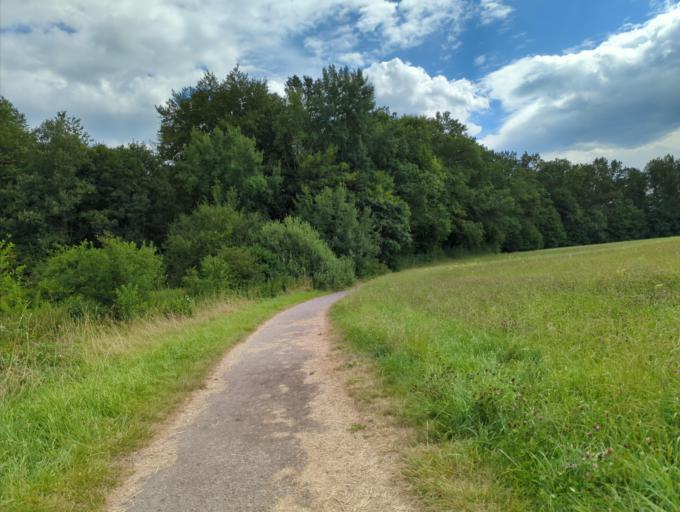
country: DE
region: Bavaria
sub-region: Upper Bavaria
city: Wasserburg am Inn
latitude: 48.0565
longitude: 12.2057
